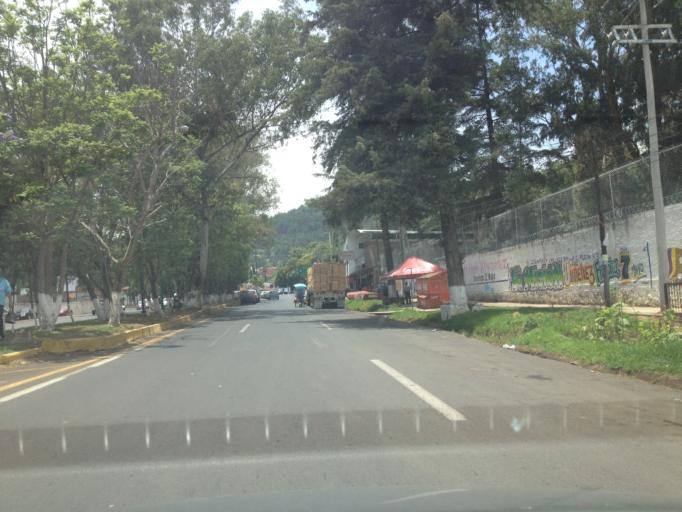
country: MX
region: Michoacan
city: Patzcuaro
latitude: 19.5290
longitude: -101.6118
